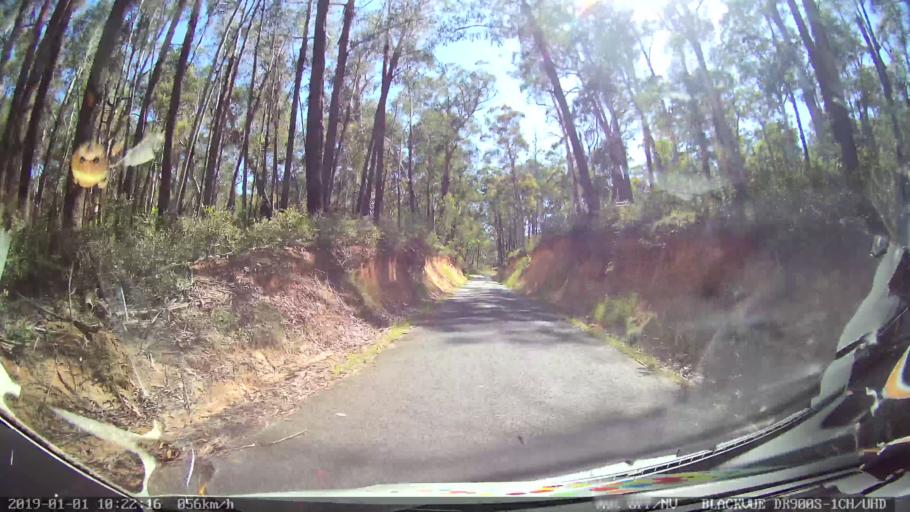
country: AU
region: New South Wales
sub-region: Snowy River
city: Jindabyne
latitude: -36.0787
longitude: 148.2024
